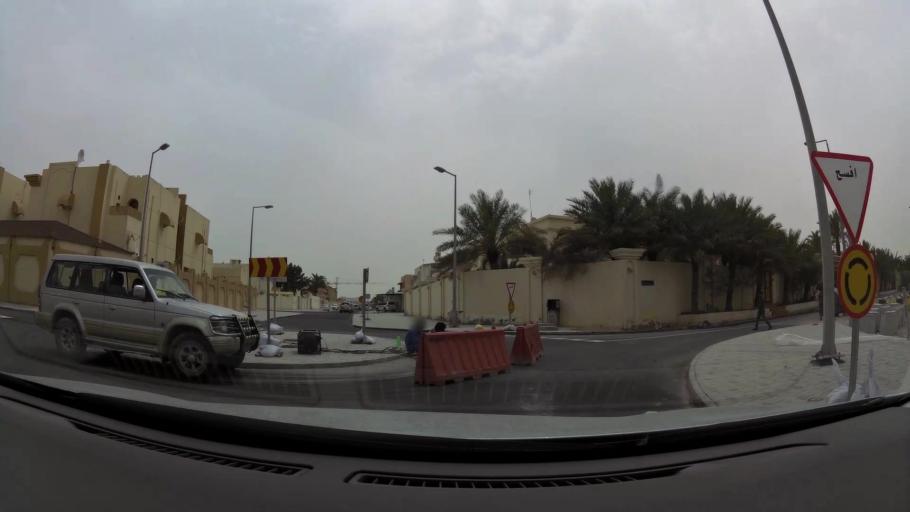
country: QA
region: Baladiyat ad Dawhah
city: Doha
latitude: 25.2451
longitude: 51.5601
